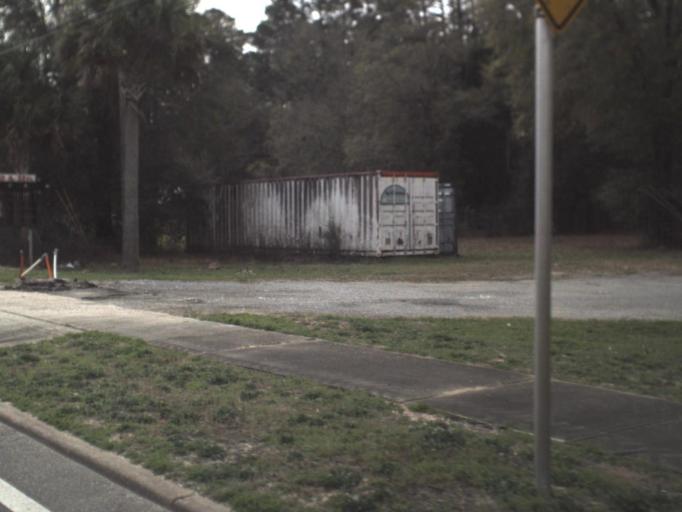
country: US
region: Florida
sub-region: Bay County
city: Youngstown
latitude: 30.4823
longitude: -85.4196
